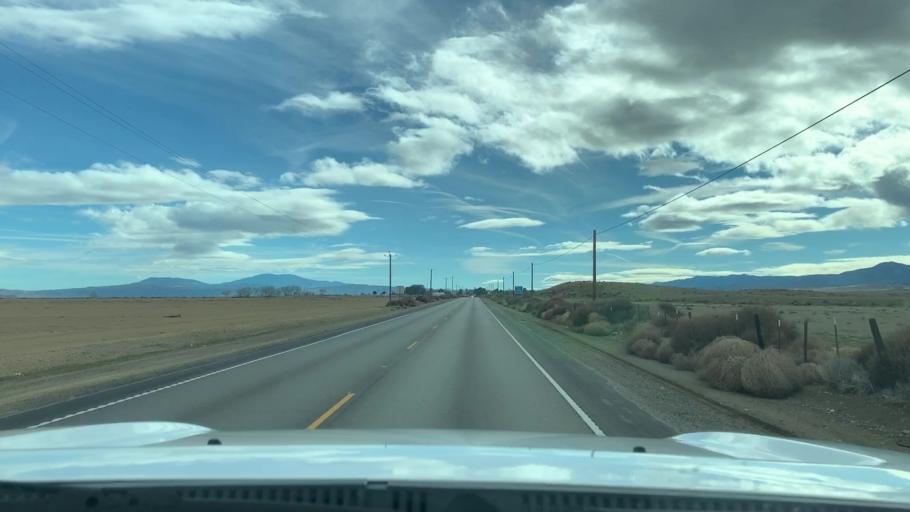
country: US
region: California
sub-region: Kern County
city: Taft Heights
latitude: 34.9560
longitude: -119.7065
